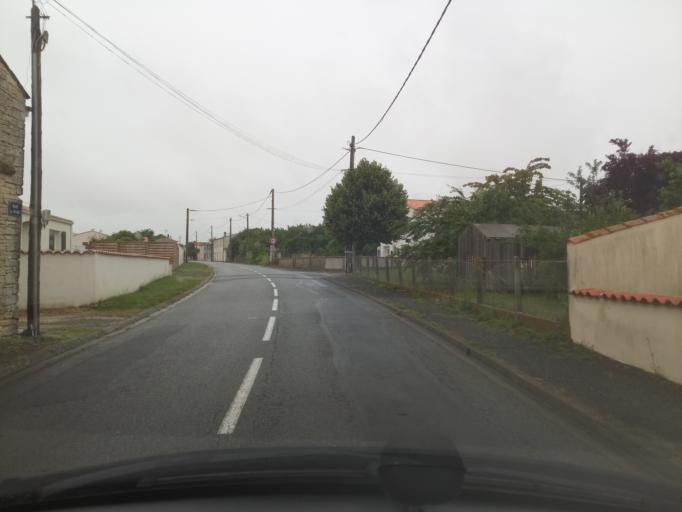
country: FR
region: Poitou-Charentes
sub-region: Departement de la Charente-Maritime
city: Andilly
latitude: 46.2319
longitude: -0.9960
